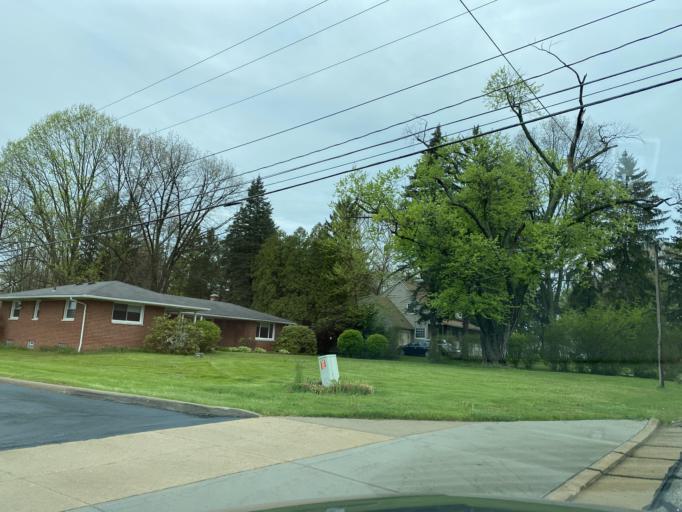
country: US
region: Ohio
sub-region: Summit County
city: Fairlawn
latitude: 41.1367
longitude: -81.6173
